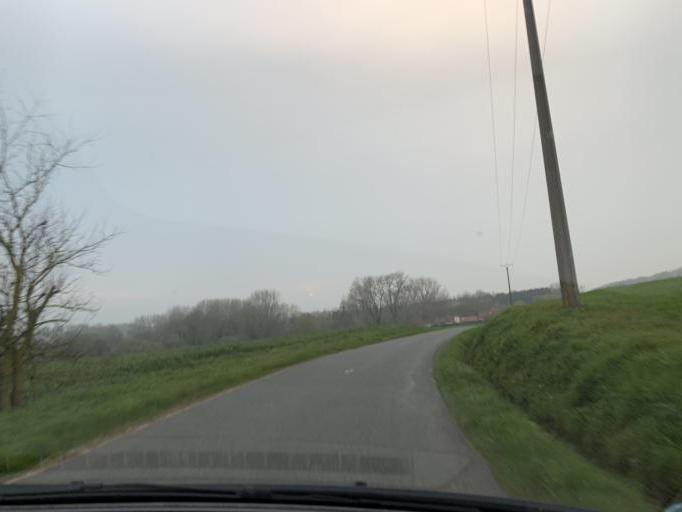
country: FR
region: Nord-Pas-de-Calais
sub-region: Departement du Pas-de-Calais
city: Wimille
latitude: 50.7621
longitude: 1.6429
